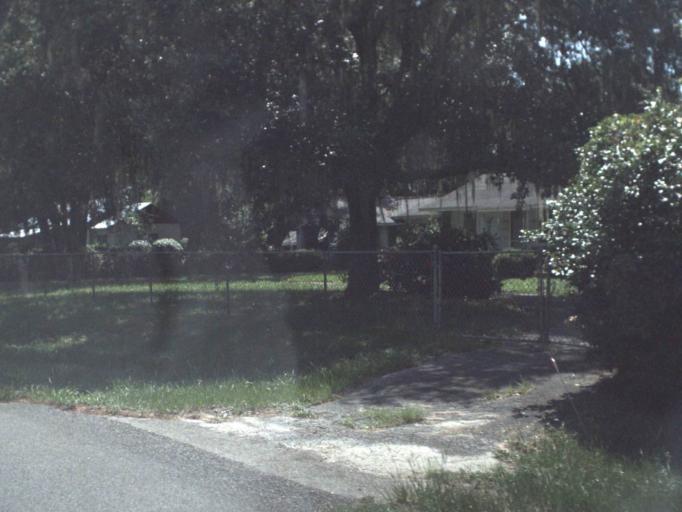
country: US
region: Florida
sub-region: Alachua County
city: Gainesville
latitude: 29.6693
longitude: -82.2457
